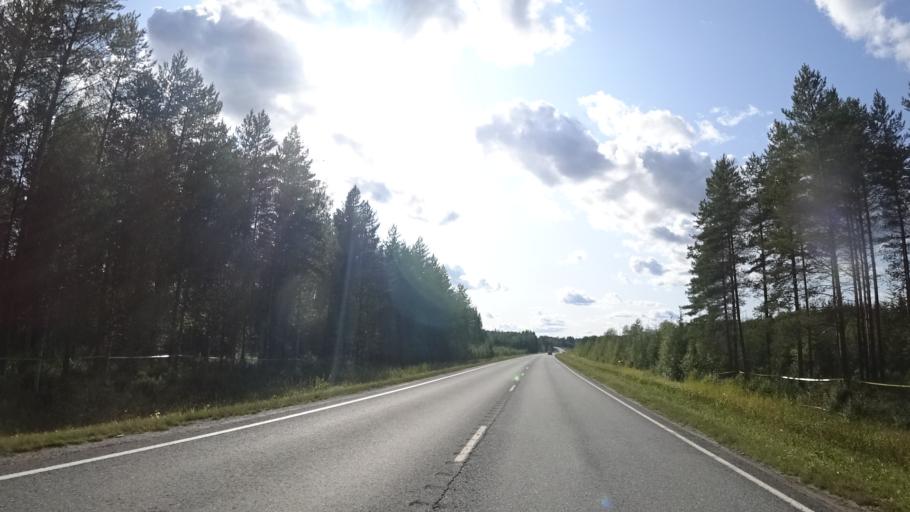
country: FI
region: North Karelia
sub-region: Keski-Karjala
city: Kitee
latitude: 62.0907
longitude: 30.0313
